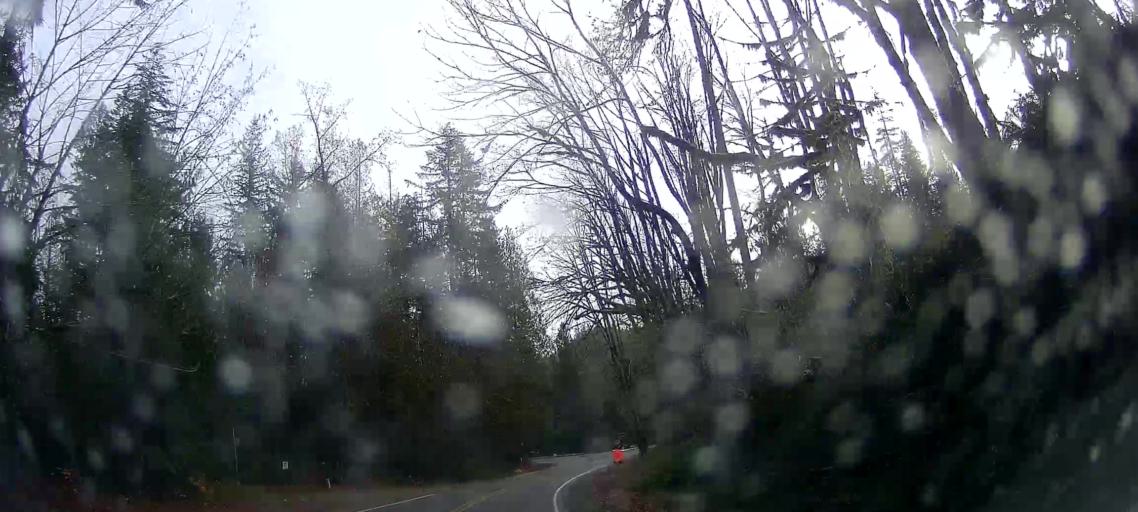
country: US
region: Washington
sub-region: Snohomish County
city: Darrington
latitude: 48.5249
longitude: -121.7732
